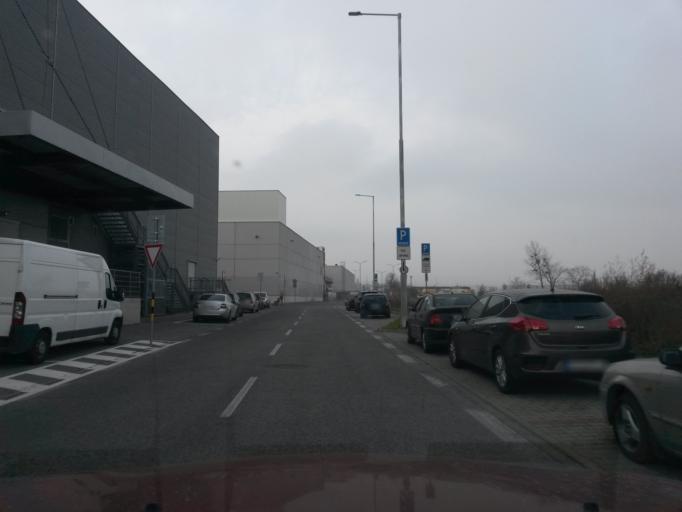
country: SK
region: Kosicky
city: Kosice
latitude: 48.6949
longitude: 21.2404
